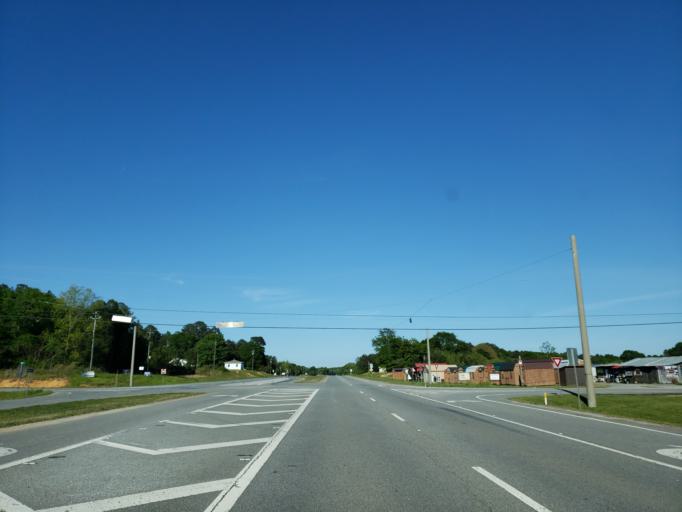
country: US
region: Georgia
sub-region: Polk County
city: Aragon
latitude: 34.0070
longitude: -85.1415
